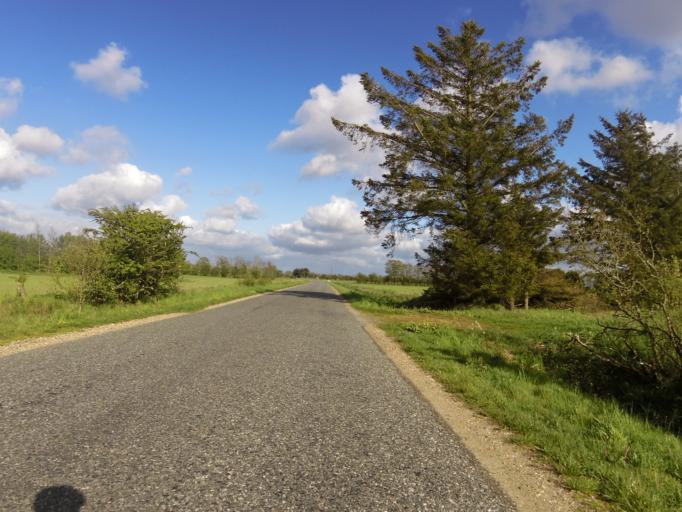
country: DK
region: South Denmark
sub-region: Esbjerg Kommune
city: Ribe
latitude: 55.2593
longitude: 8.7866
